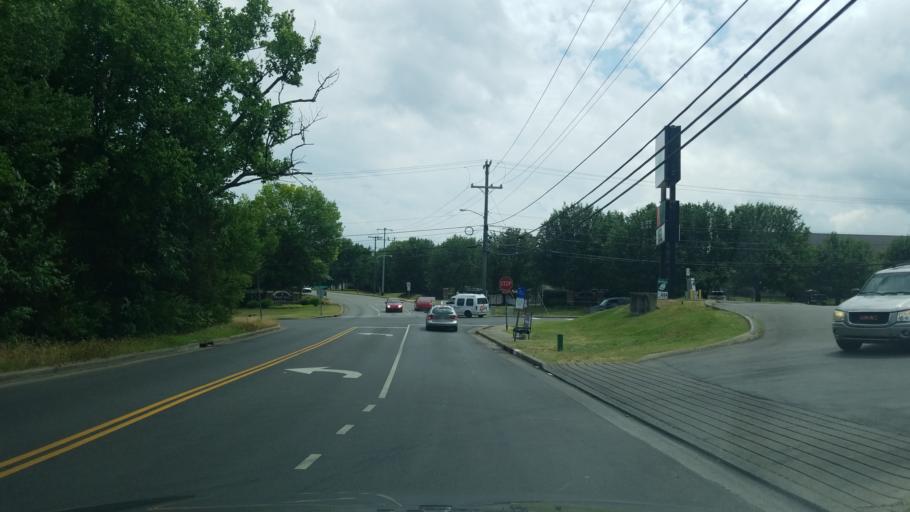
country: US
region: Tennessee
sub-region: Rutherford County
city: La Vergne
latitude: 36.0882
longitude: -86.6071
